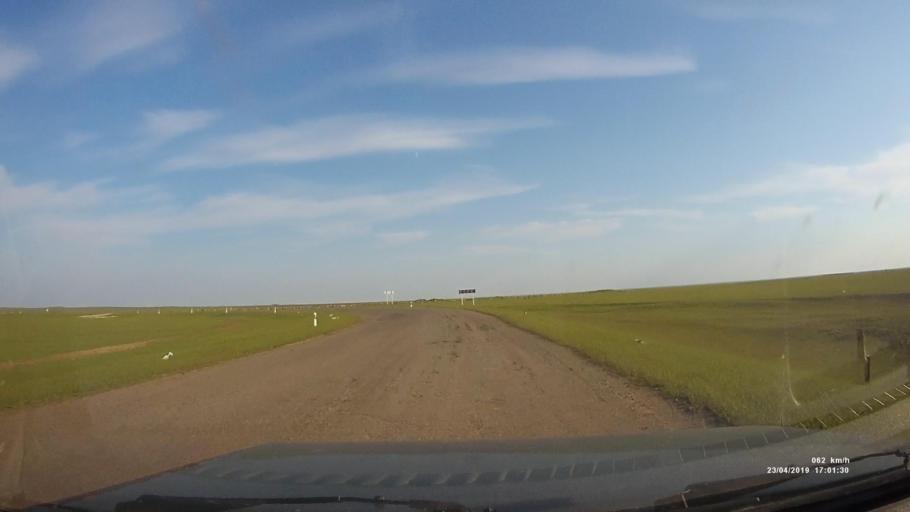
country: RU
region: Kalmykiya
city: Priyutnoye
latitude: 46.2955
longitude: 43.4081
